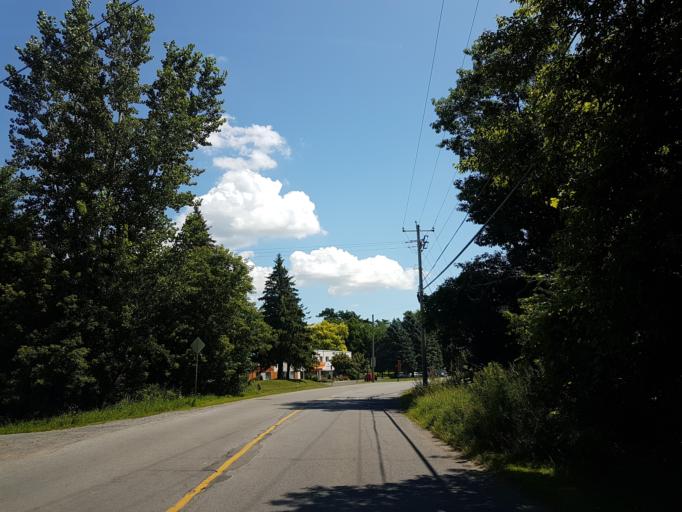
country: CA
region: Quebec
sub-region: Mauricie
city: Nicolet
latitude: 46.2332
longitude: -72.6325
